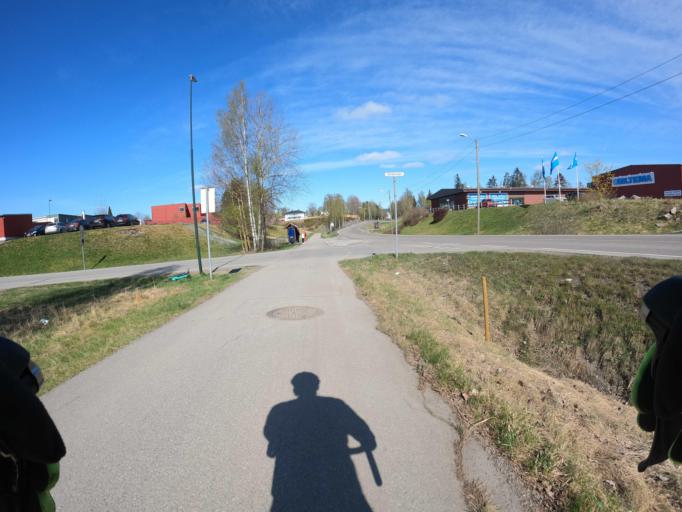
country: NO
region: Akershus
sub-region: Skedsmo
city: Lillestrom
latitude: 59.9726
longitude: 11.0058
